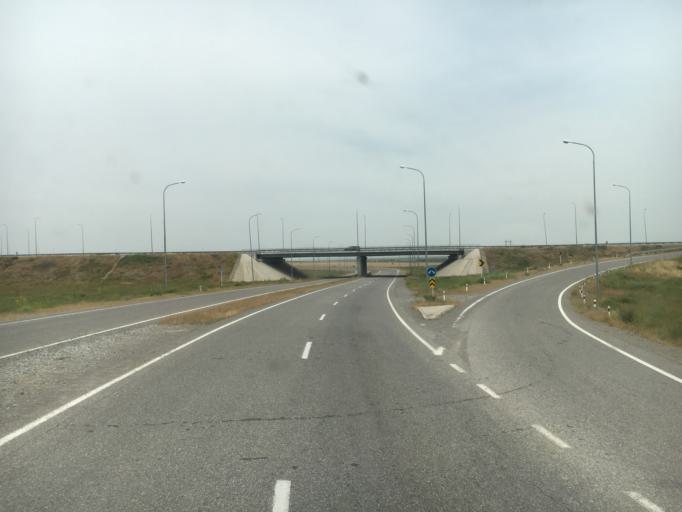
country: KZ
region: Ongtustik Qazaqstan
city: Temirlanovka
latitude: 42.5271
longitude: 69.3444
